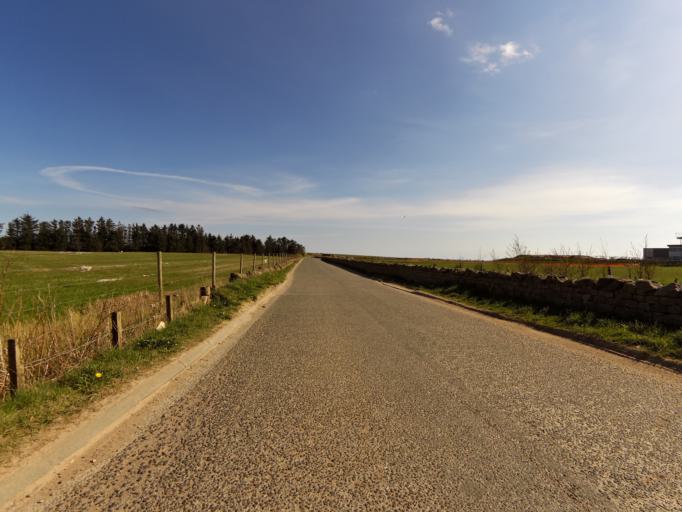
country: GB
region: Scotland
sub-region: Aberdeenshire
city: Portlethen
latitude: 57.0932
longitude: -2.1012
